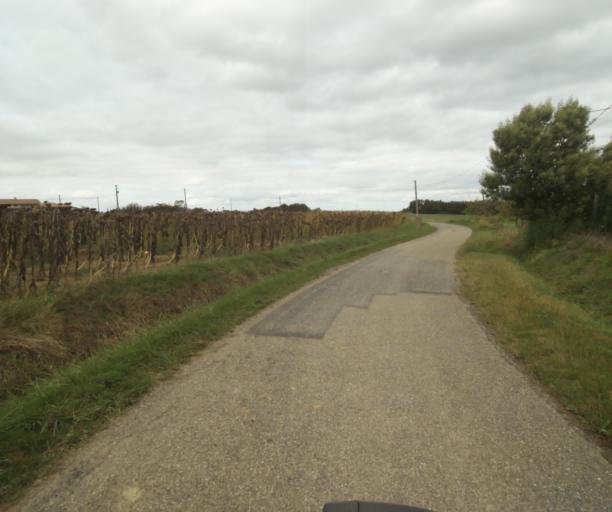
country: FR
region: Midi-Pyrenees
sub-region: Departement du Tarn-et-Garonne
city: Beaumont-de-Lomagne
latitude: 43.8471
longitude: 1.0978
